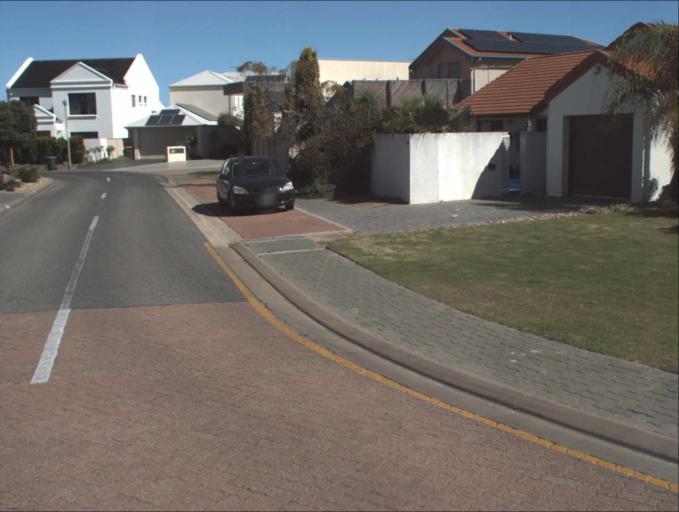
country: AU
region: South Australia
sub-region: Port Adelaide Enfield
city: Birkenhead
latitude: -34.7961
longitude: 138.4883
